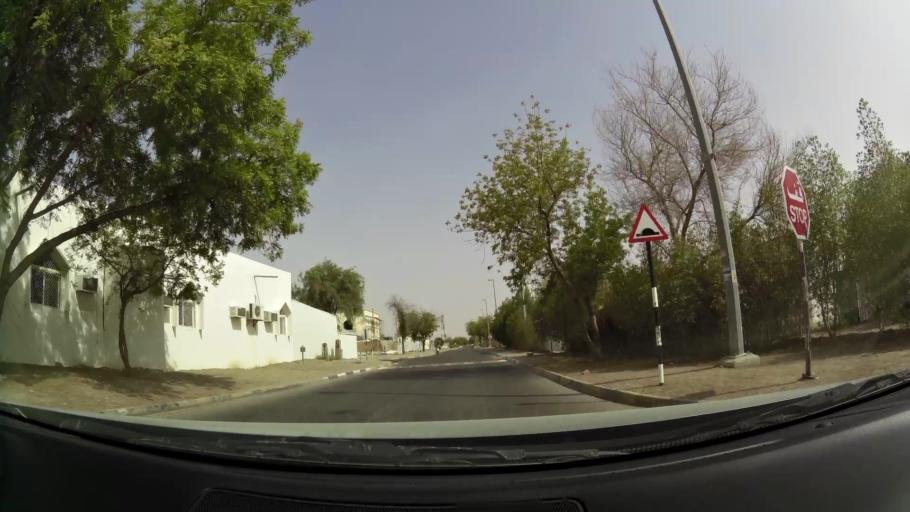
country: AE
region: Abu Dhabi
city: Al Ain
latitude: 24.1943
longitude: 55.6349
